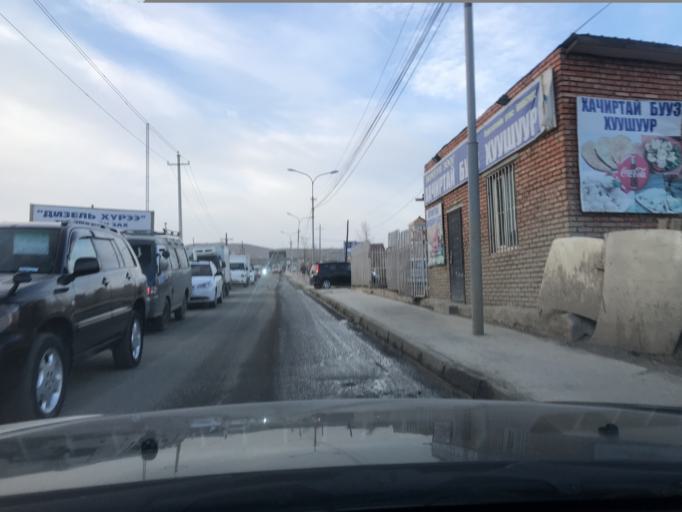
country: MN
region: Ulaanbaatar
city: Ulaanbaatar
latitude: 47.9282
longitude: 106.9979
